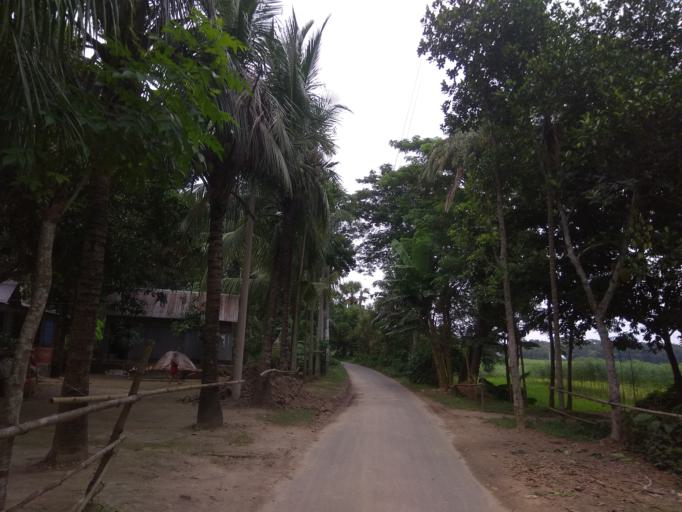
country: BD
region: Dhaka
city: Dohar
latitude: 23.4844
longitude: 90.0191
